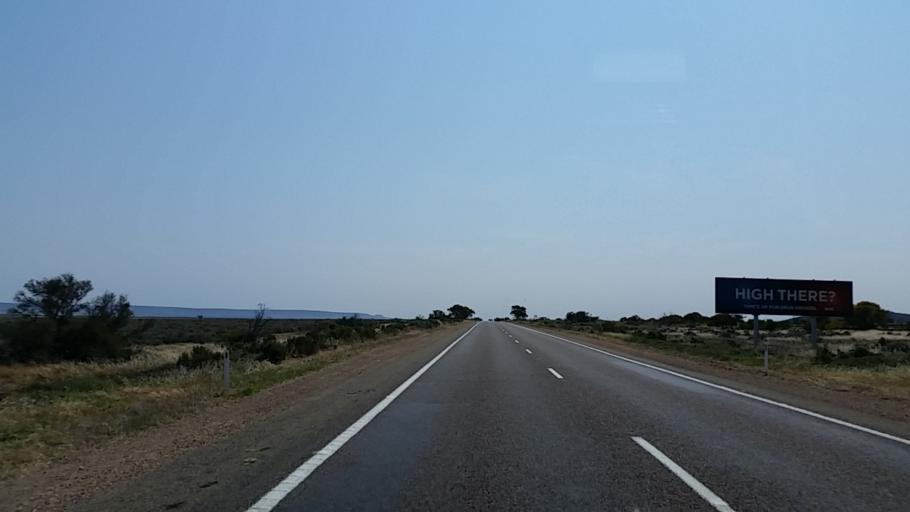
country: AU
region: South Australia
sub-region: Port Pirie City and Dists
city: Port Pirie
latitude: -32.8176
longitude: 137.9724
